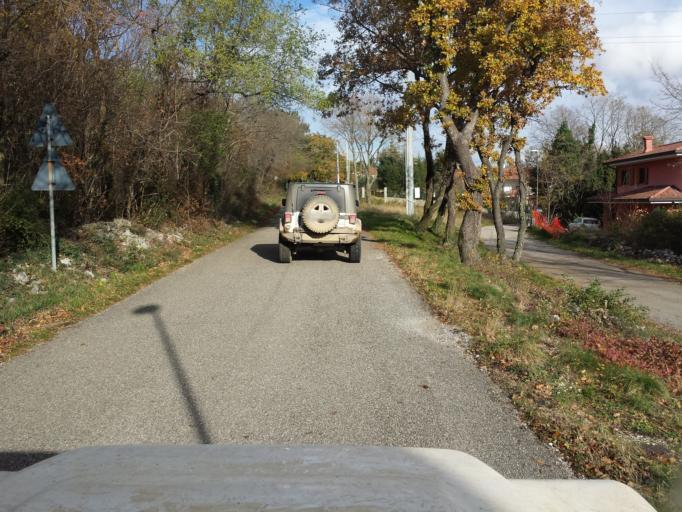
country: IT
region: Friuli Venezia Giulia
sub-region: Provincia di Gorizia
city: Doberdo del Lago
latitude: 45.8773
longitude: 13.5577
